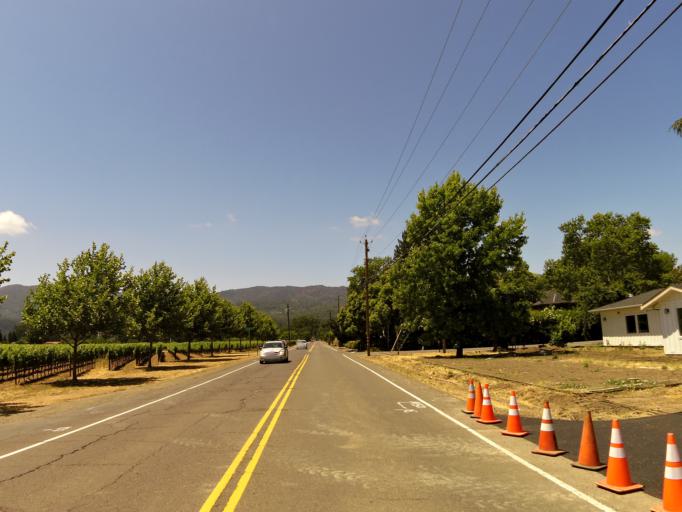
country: US
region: California
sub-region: Napa County
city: Saint Helena
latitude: 38.4858
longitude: -122.4382
